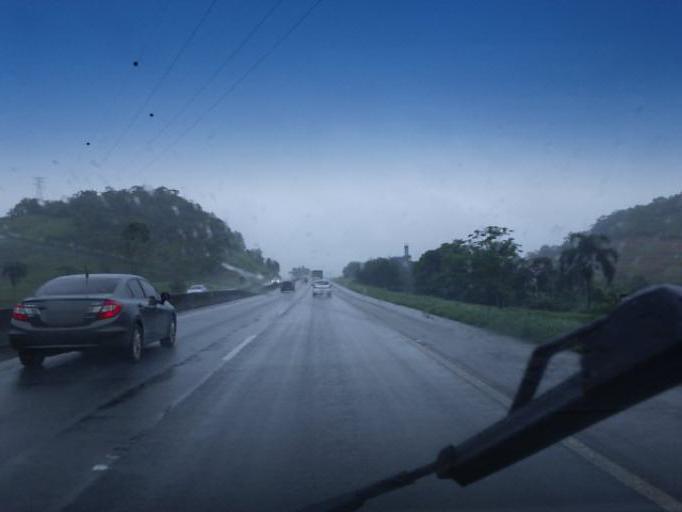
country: BR
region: Santa Catarina
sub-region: Joinville
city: Joinville
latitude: -26.1169
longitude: -48.8786
